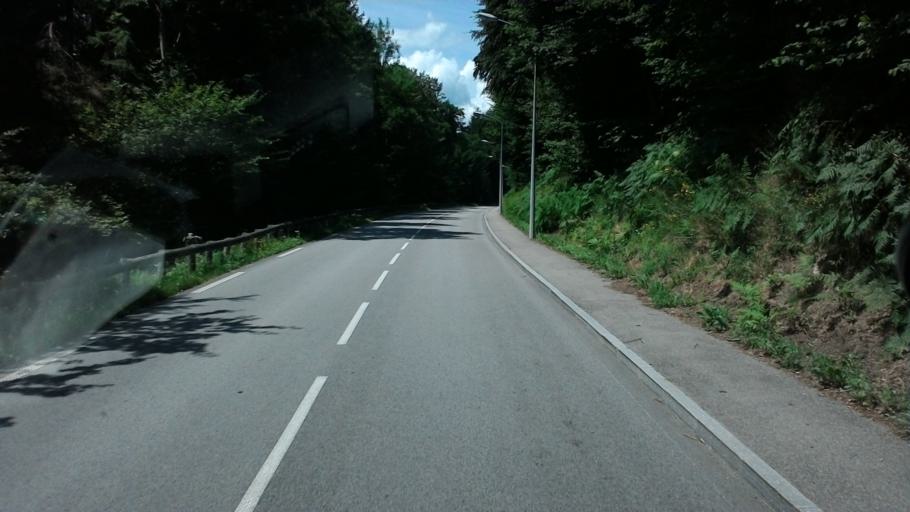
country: FR
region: Lorraine
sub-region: Departement des Vosges
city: Le Tholy
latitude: 48.0844
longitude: 6.7383
